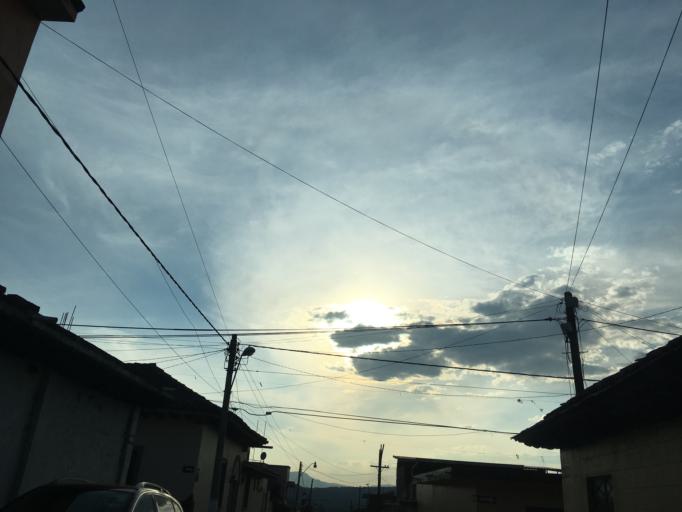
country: MX
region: Michoacan
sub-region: Tingueindin
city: Tingueindin
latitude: 19.7411
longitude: -102.4813
